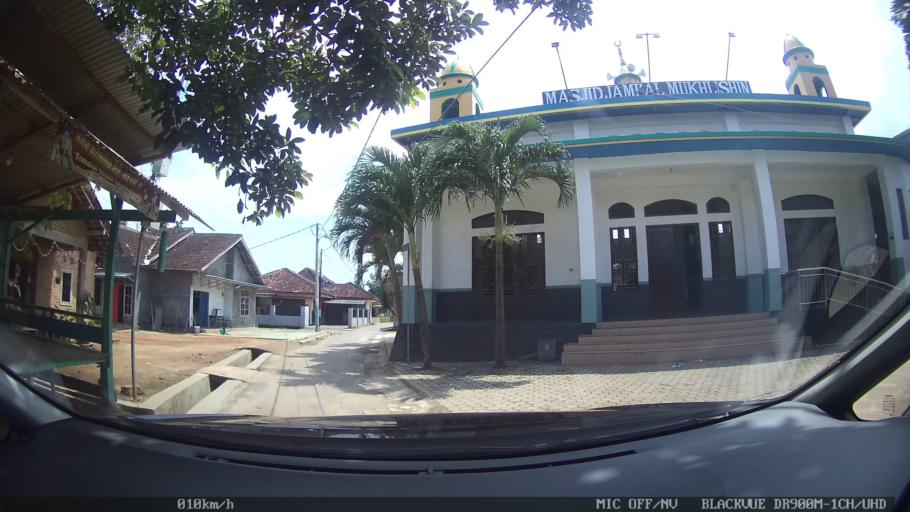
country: ID
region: Lampung
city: Kedaton
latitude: -5.3714
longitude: 105.3056
